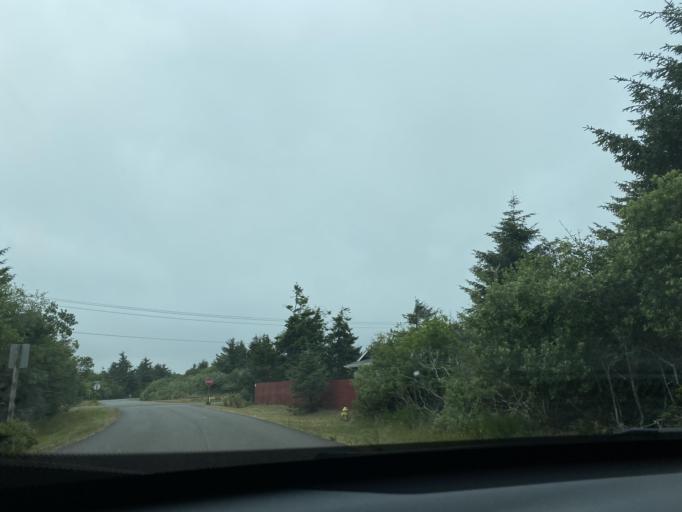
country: US
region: Washington
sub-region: Grays Harbor County
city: Ocean Shores
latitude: 46.9520
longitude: -124.1449
